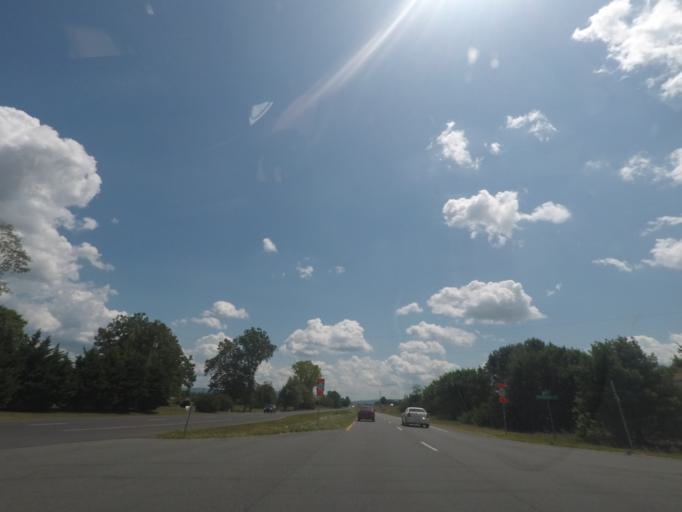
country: US
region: Virginia
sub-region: City of Winchester
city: Winchester
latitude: 39.0927
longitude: -78.1000
